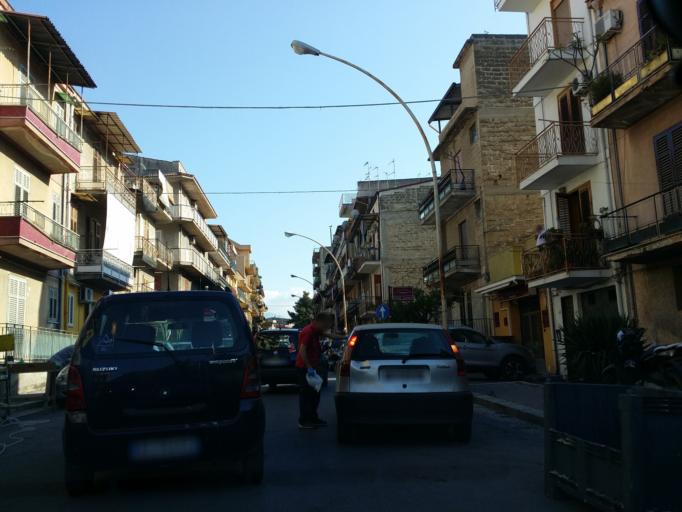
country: IT
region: Sicily
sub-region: Palermo
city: Misilmeri
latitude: 38.0274
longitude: 13.4484
